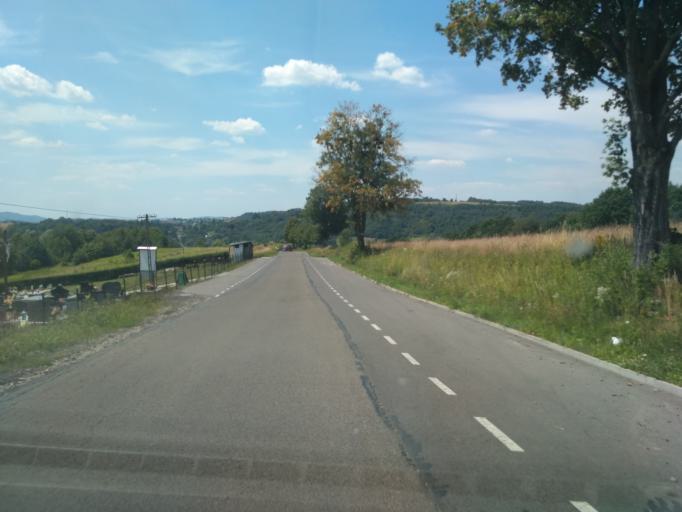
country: PL
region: Subcarpathian Voivodeship
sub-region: Powiat strzyzowski
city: Strzyzow
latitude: 49.8735
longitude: 21.8283
